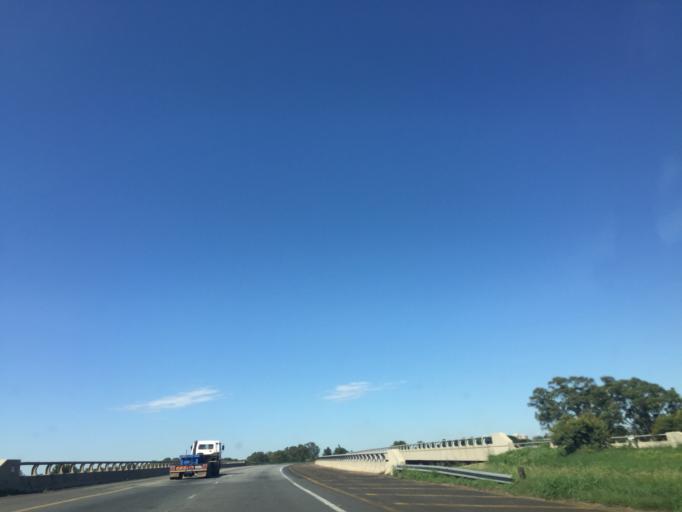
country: ZA
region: Gauteng
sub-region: Sedibeng District Municipality
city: Vereeniging
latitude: -26.6481
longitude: 27.9370
